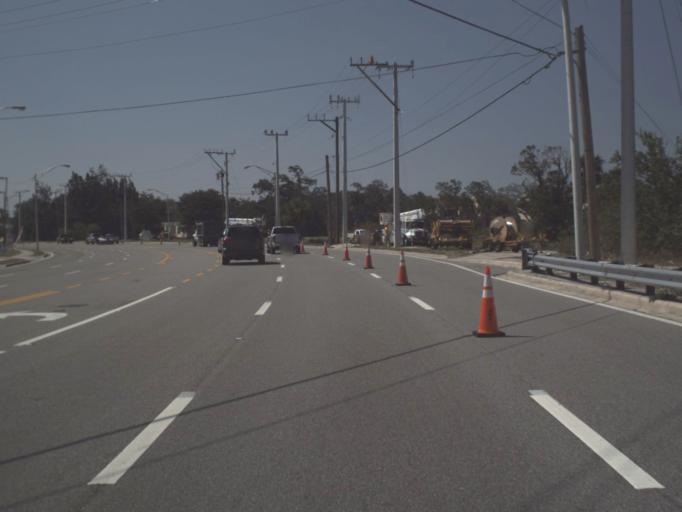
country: US
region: Florida
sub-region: Brevard County
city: Melbourne
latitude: 28.1143
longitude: -80.6201
